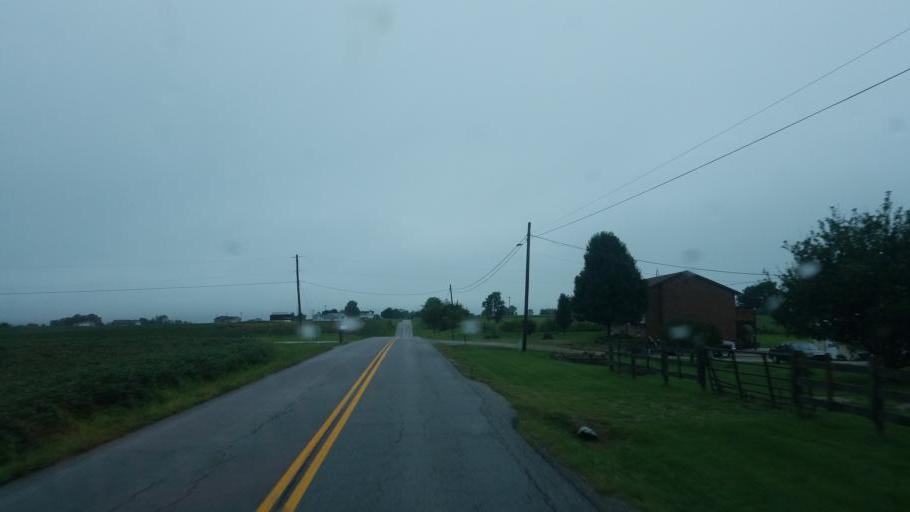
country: US
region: Kentucky
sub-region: Fleming County
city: Flemingsburg
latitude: 38.4131
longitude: -83.6628
